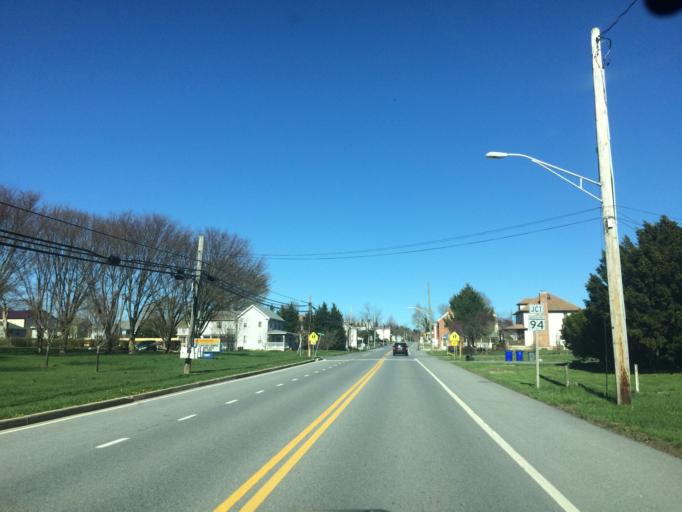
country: US
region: Maryland
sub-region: Carroll County
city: Mount Airy
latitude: 39.3355
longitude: -77.0681
